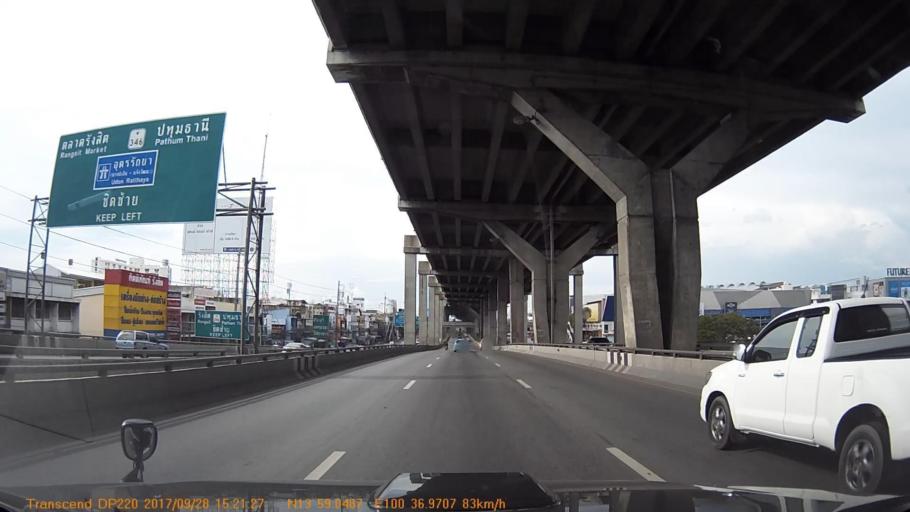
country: TH
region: Phra Nakhon Si Ayutthaya
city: Ban Bang Kadi Pathum Thani
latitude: 13.9845
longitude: 100.6161
